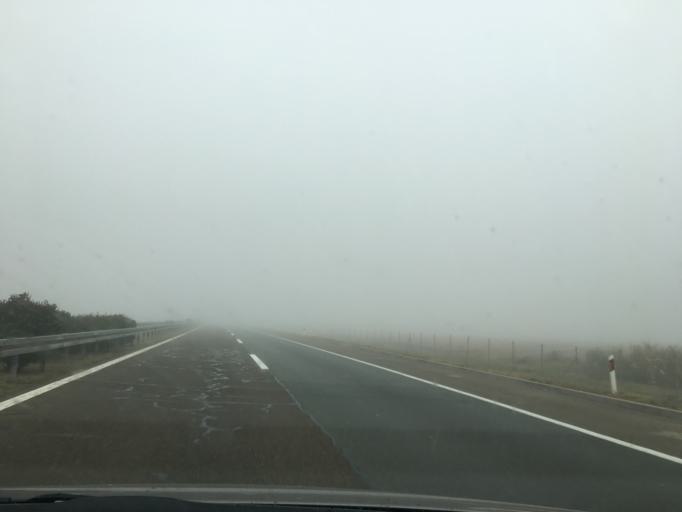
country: RS
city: Novi Karlovci
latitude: 45.0505
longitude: 20.1737
